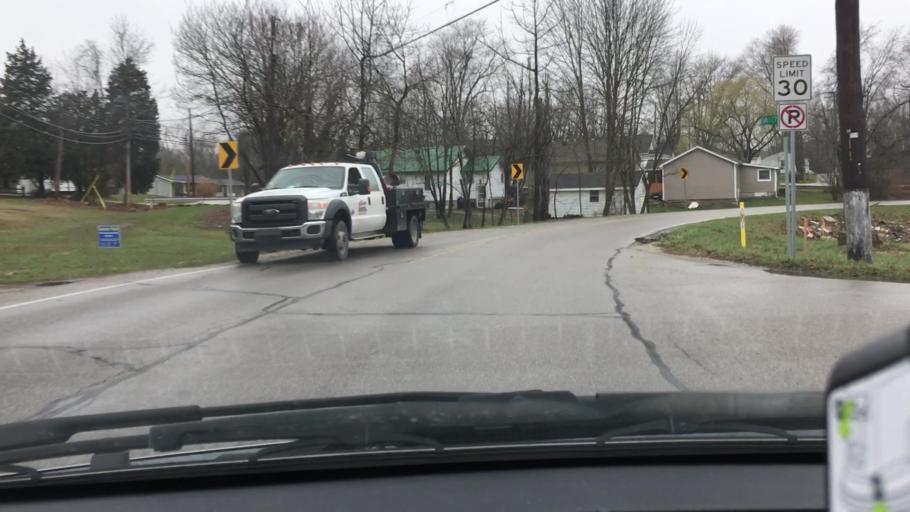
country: US
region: Indiana
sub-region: Lawrence County
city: Bedford
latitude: 38.8737
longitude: -86.4766
